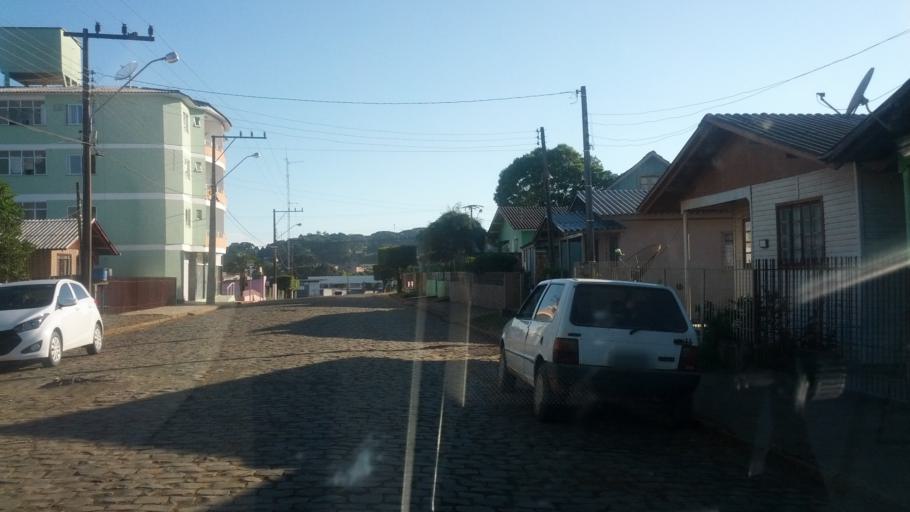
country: BR
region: Rio Grande do Sul
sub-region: Vacaria
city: Estrela
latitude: -27.8998
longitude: -50.7613
